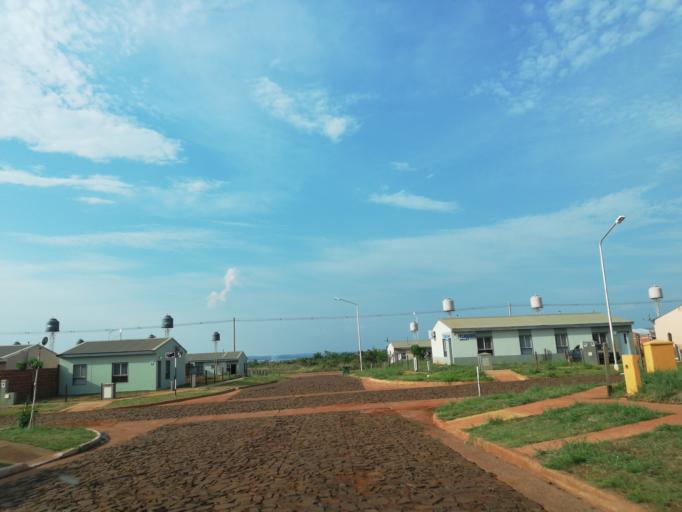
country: AR
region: Misiones
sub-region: Departamento de Capital
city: Posadas
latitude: -27.3997
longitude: -55.9857
